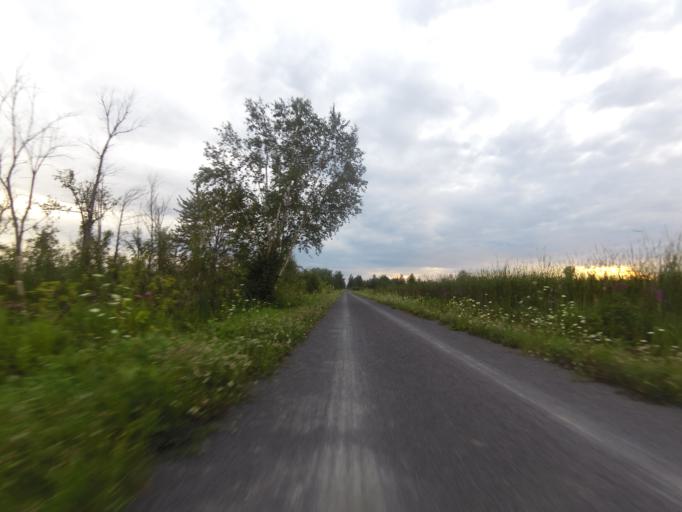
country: CA
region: Ontario
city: Carleton Place
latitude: 45.1856
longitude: -76.0357
